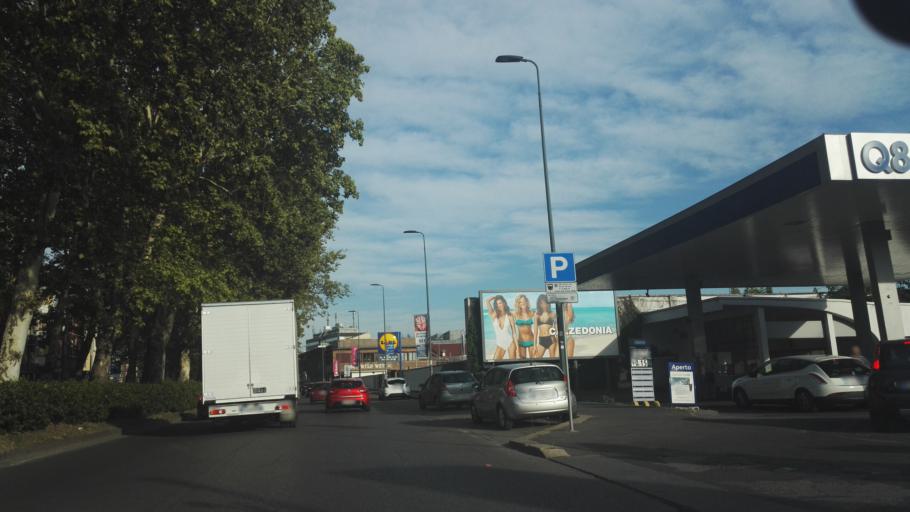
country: IT
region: Lombardy
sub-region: Citta metropolitana di Milano
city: Milano
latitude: 45.4461
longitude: 9.1597
